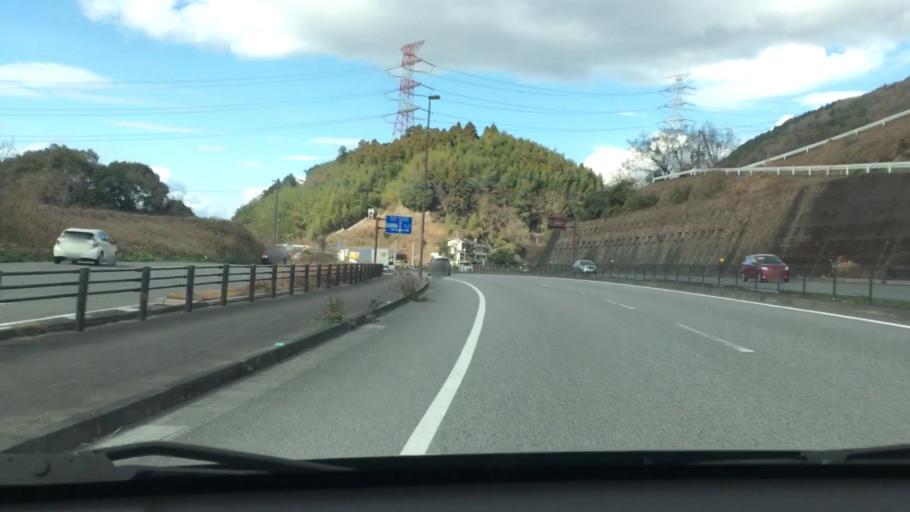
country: JP
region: Oita
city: Oita
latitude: 33.1110
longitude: 131.6568
